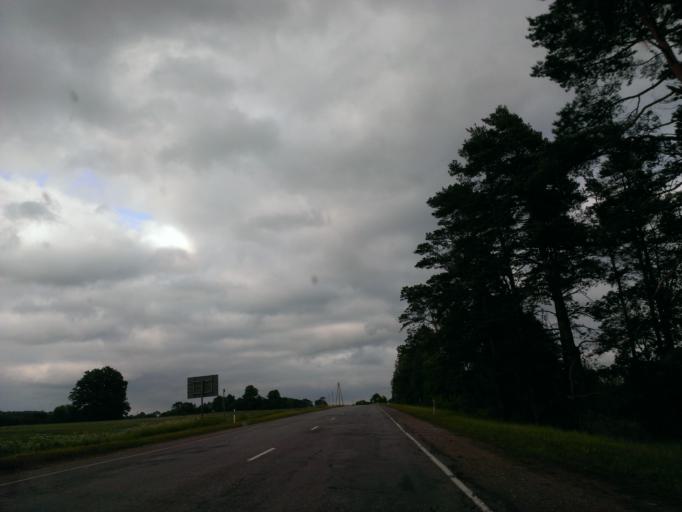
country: LV
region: Skrunda
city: Skrunda
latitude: 56.6774
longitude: 22.2084
